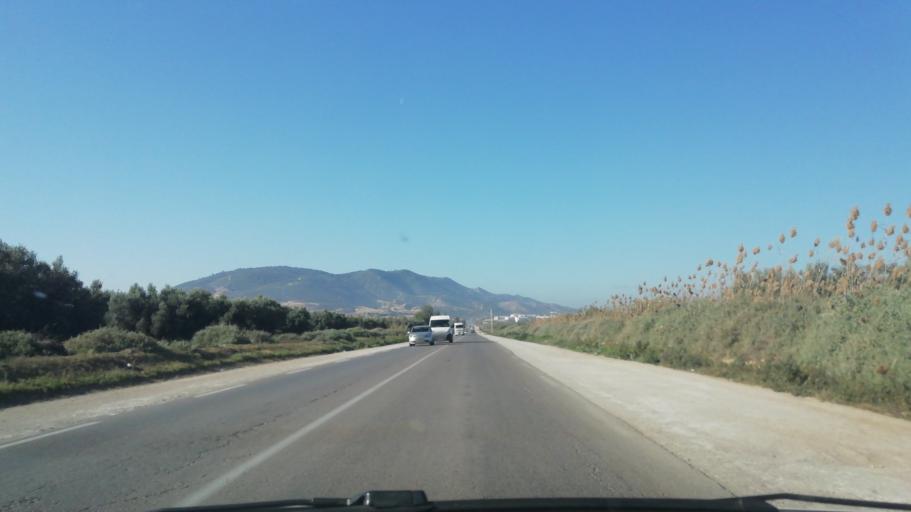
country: DZ
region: Mascara
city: Sig
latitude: 35.5394
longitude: -0.1328
